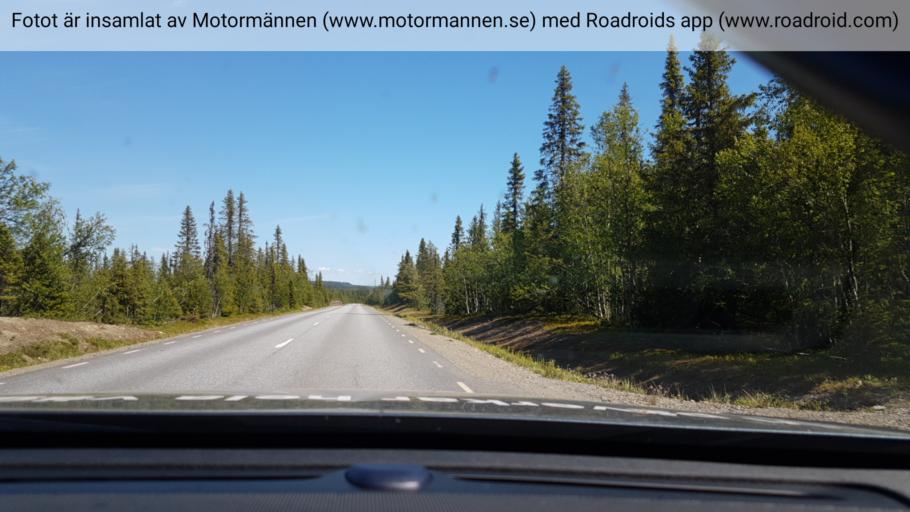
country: SE
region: Vaesterbotten
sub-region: Asele Kommun
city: Insjon
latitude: 64.7298
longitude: 17.4742
